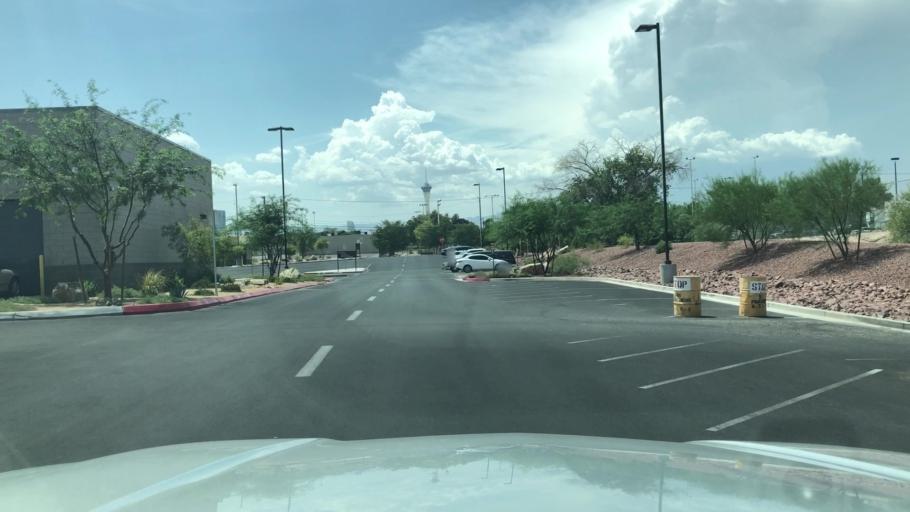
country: US
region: Nevada
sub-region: Clark County
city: Winchester
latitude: 36.1467
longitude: -115.1128
